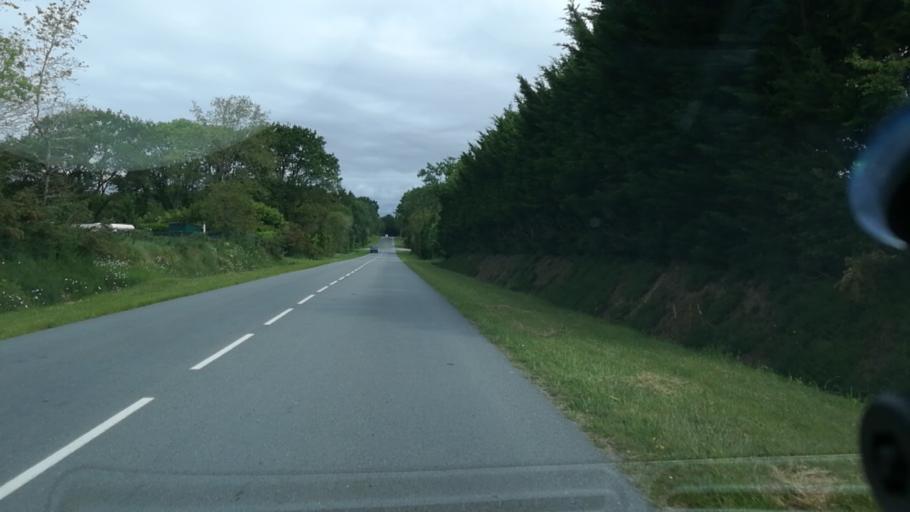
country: FR
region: Brittany
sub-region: Departement du Morbihan
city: Penestin
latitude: 47.4632
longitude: -2.4780
